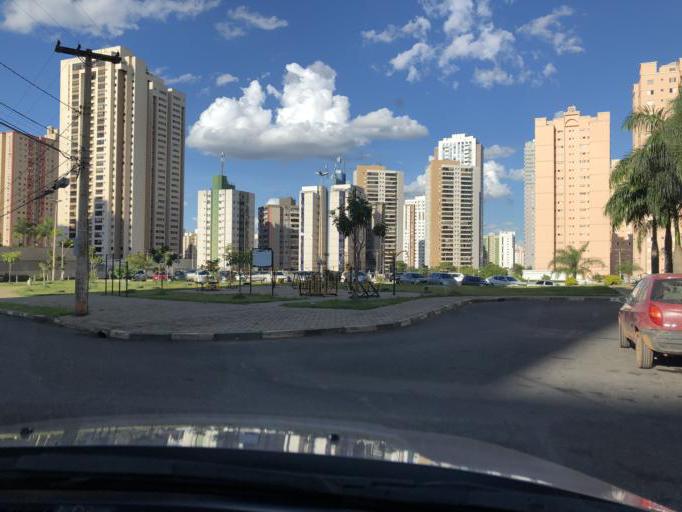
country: BR
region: Federal District
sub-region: Brasilia
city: Brasilia
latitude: -15.8455
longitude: -48.0280
